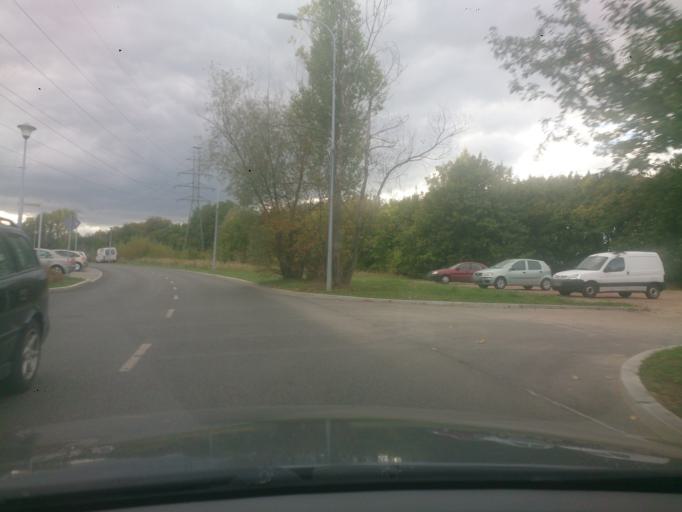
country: PL
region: Kujawsko-Pomorskie
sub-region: Grudziadz
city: Grudziadz
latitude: 53.4683
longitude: 18.7314
